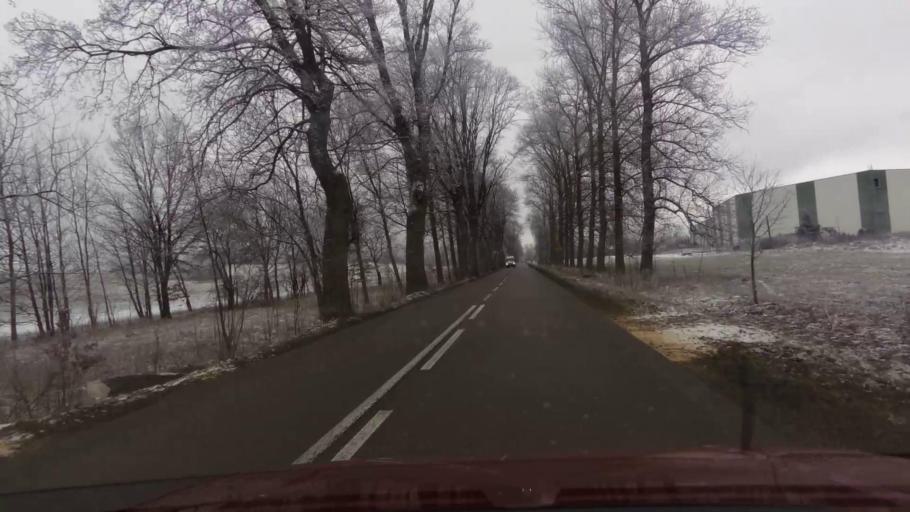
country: PL
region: West Pomeranian Voivodeship
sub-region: Powiat swidwinski
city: Polczyn-Zdroj
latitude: 53.7926
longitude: 16.0308
